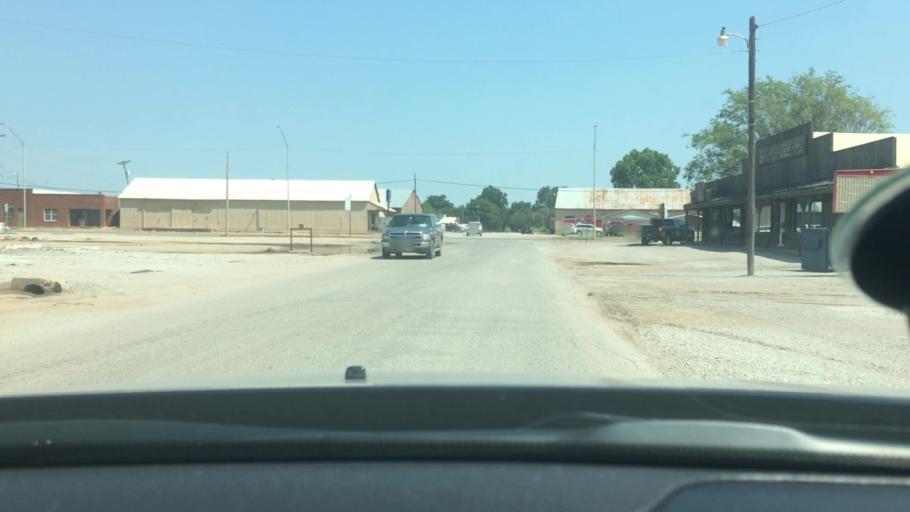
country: US
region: Oklahoma
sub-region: Garvin County
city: Lindsay
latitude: 34.8360
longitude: -97.6013
